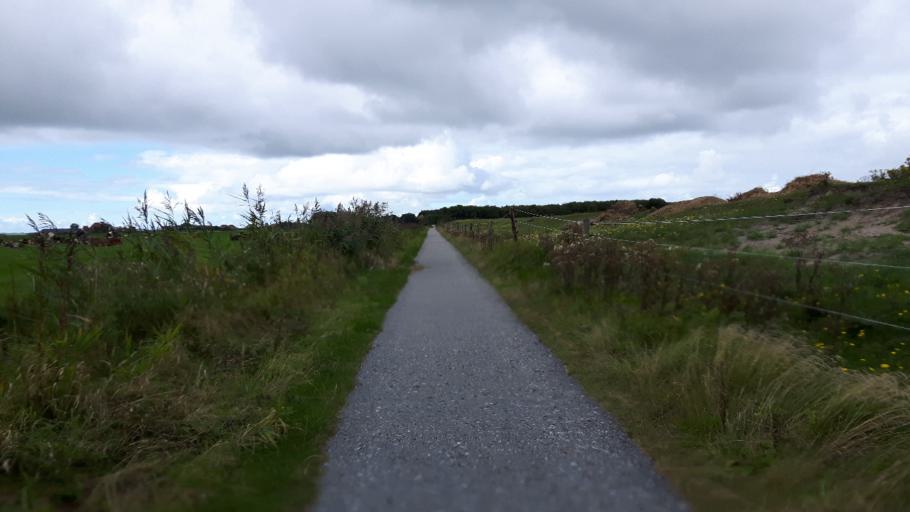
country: NL
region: Friesland
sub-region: Gemeente Ameland
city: Hollum
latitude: 53.4438
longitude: 5.6747
